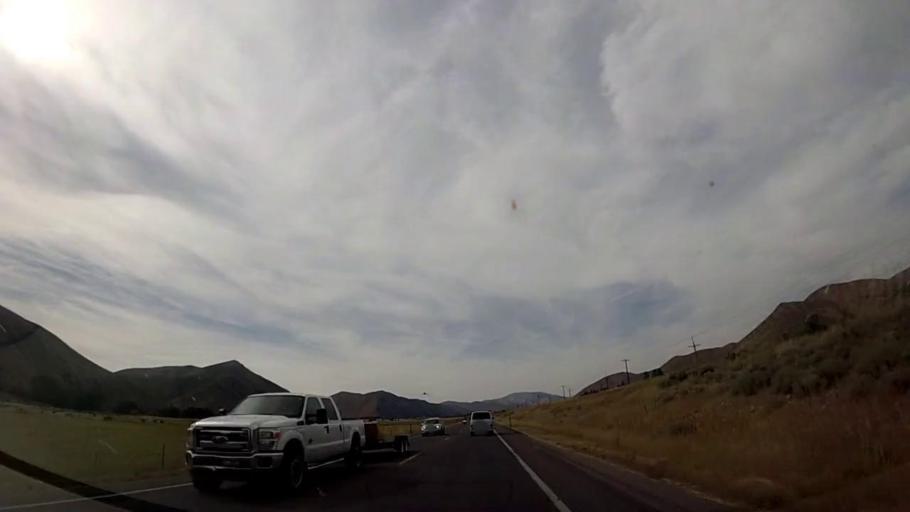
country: US
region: Idaho
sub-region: Blaine County
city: Bellevue
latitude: 43.4924
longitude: -114.2827
